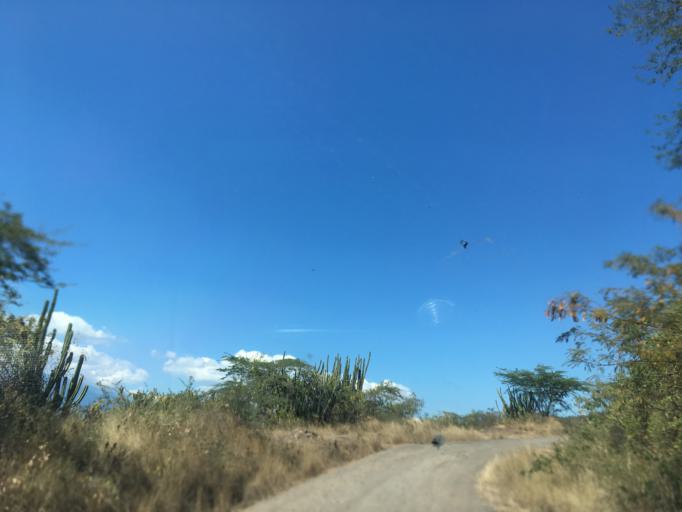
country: CO
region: Santander
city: Barichara
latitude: 6.6345
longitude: -73.2484
